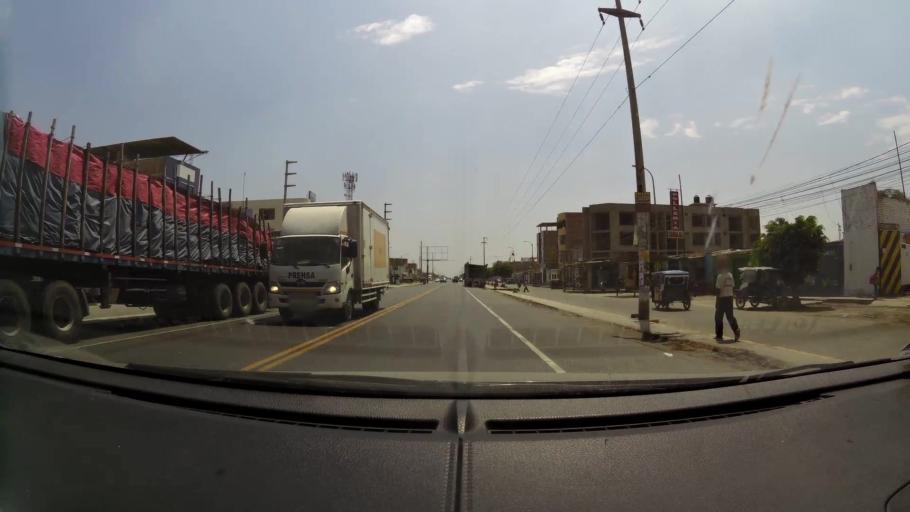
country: PE
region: La Libertad
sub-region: Chepen
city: Pacanga
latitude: -7.1565
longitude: -79.4436
